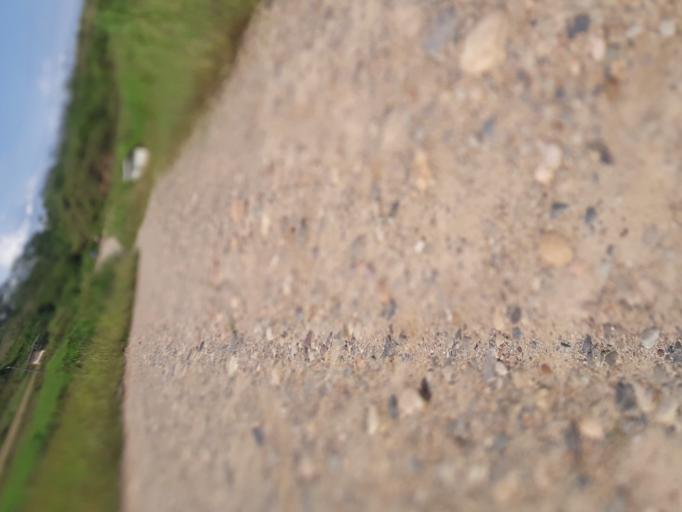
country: EC
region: Napo
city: Tena
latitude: -0.9675
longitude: -77.8163
